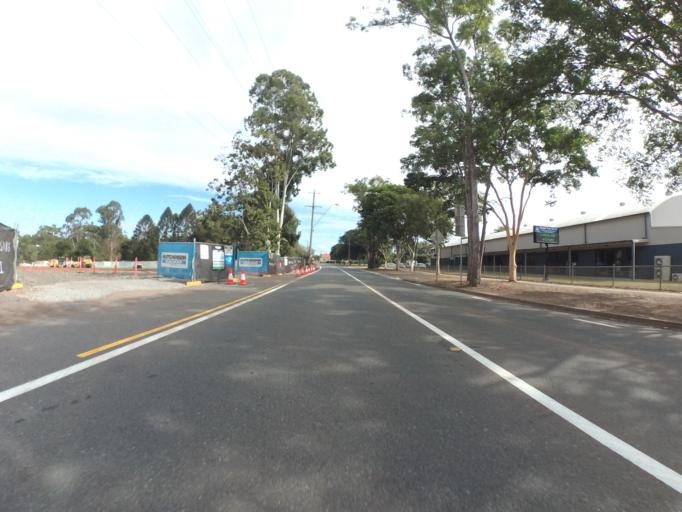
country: AU
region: Queensland
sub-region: Brisbane
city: Moggill
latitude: -27.5695
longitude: 152.8771
